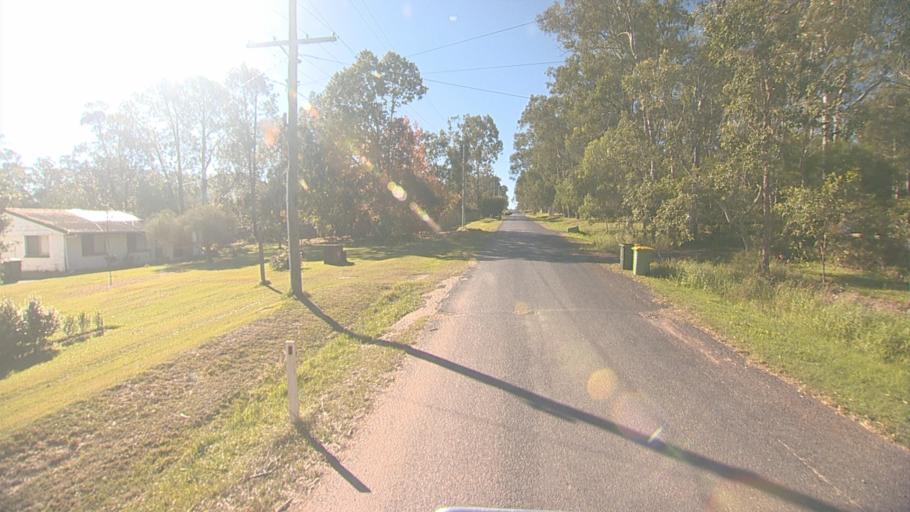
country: AU
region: Queensland
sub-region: Logan
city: Park Ridge South
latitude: -27.7318
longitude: 153.0112
